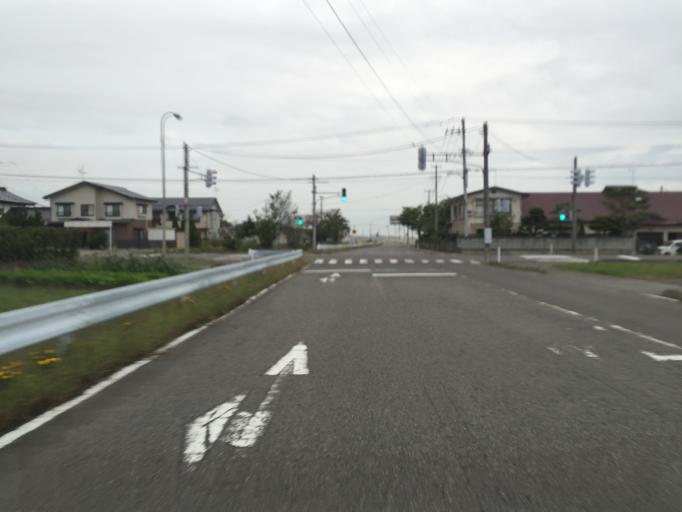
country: JP
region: Fukushima
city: Kitakata
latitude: 37.5542
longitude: 139.8720
